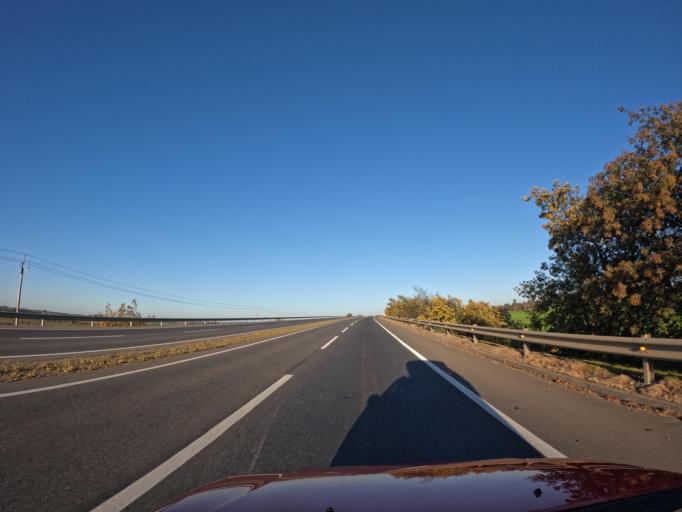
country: CL
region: Biobio
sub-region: Provincia de Nuble
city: Bulnes
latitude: -36.6588
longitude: -72.2714
